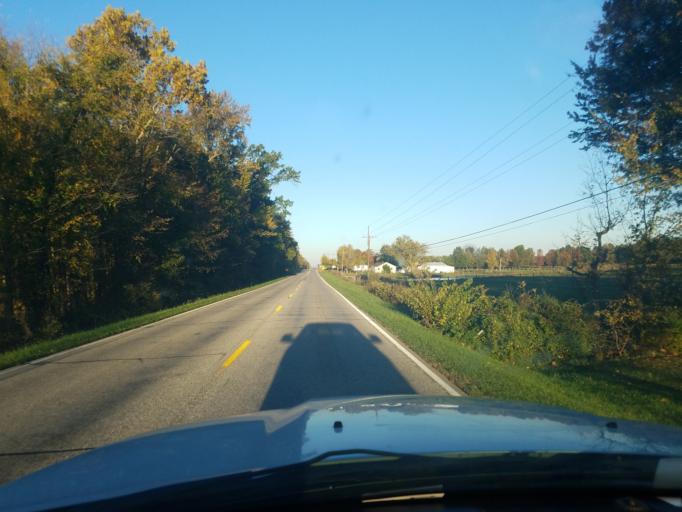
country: US
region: Indiana
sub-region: Washington County
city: New Pekin
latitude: 38.3997
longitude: -86.0834
